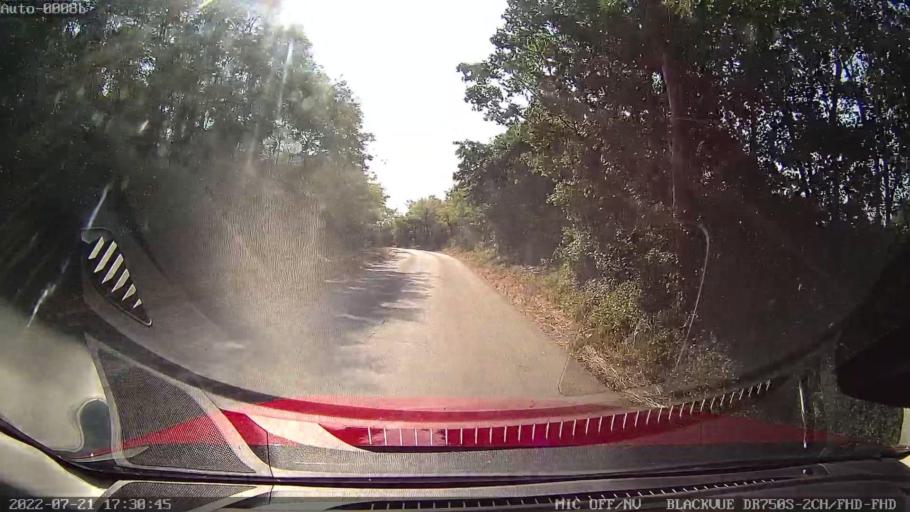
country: HR
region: Istarska
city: Karojba
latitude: 45.1754
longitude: 13.7715
